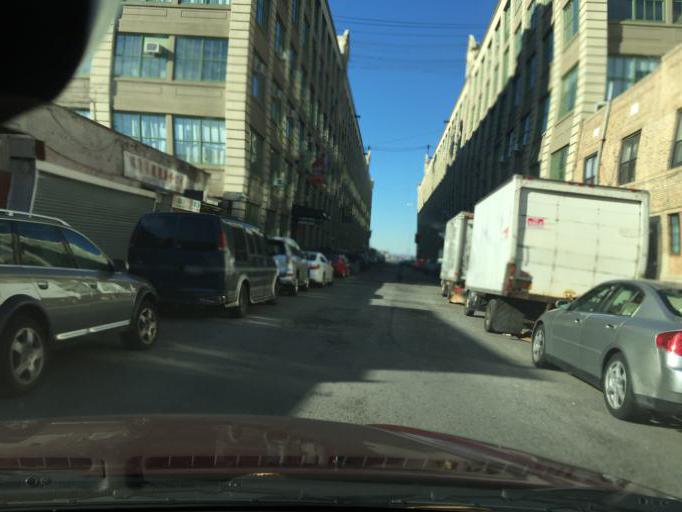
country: US
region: New York
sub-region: Kings County
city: Bensonhurst
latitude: 40.6557
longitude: -74.0067
